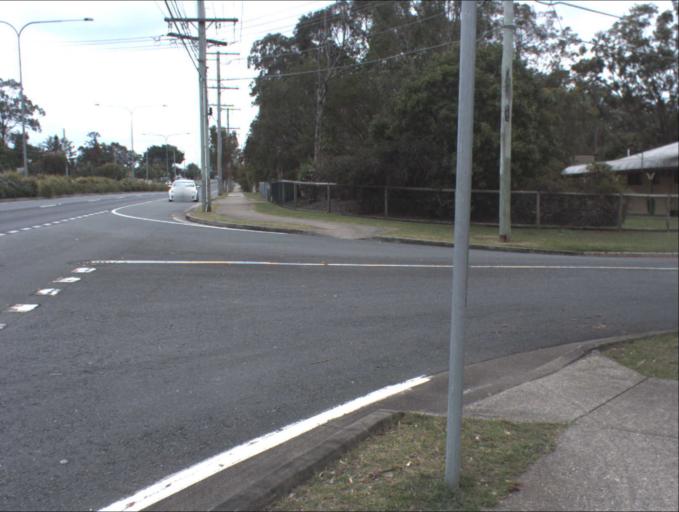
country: AU
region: Queensland
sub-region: Logan
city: Waterford West
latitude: -27.6888
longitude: 153.1247
